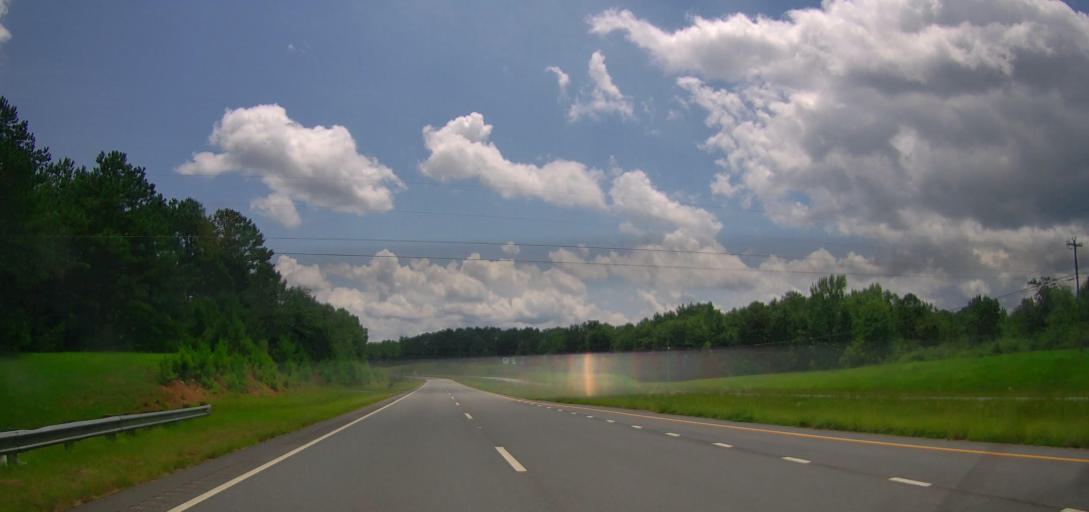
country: US
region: Georgia
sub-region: Upson County
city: Thomaston
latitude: 32.8310
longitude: -84.3082
